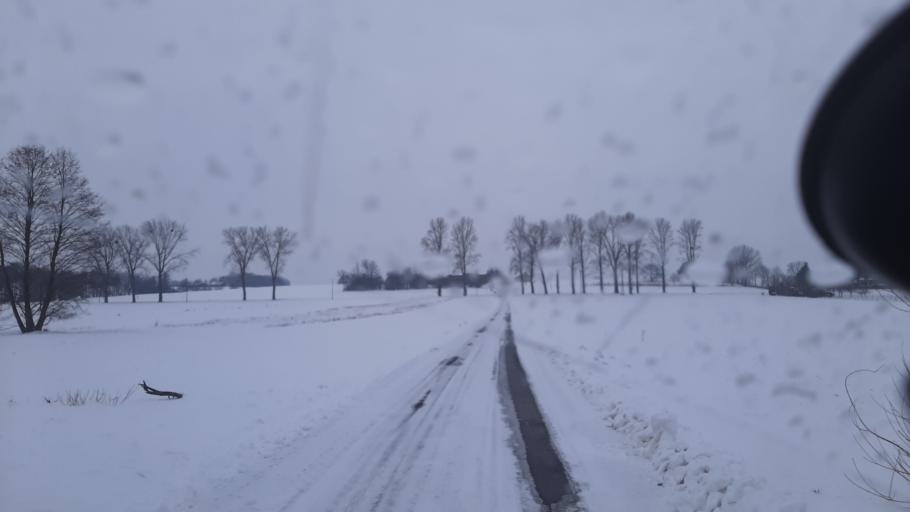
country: PL
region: Lublin Voivodeship
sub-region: Powiat lubelski
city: Jastkow
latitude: 51.3476
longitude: 22.3919
